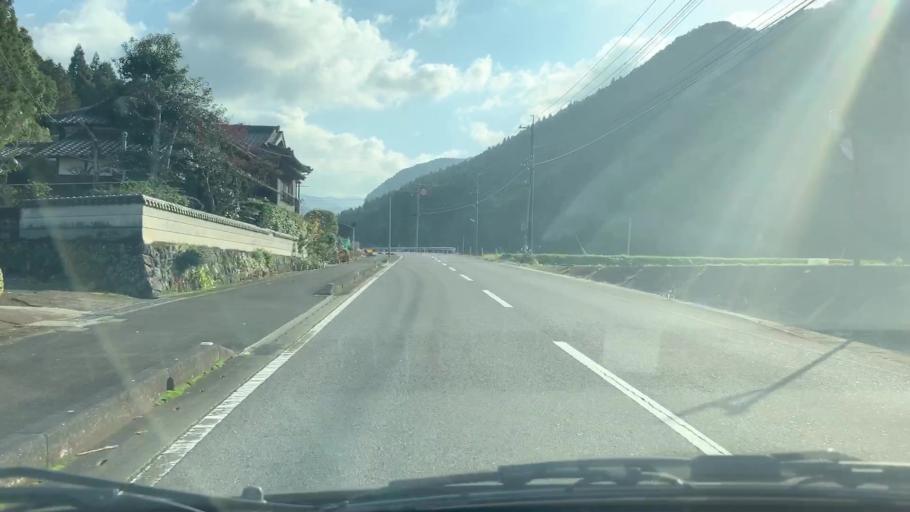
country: JP
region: Saga Prefecture
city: Kashima
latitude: 33.0609
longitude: 130.0700
